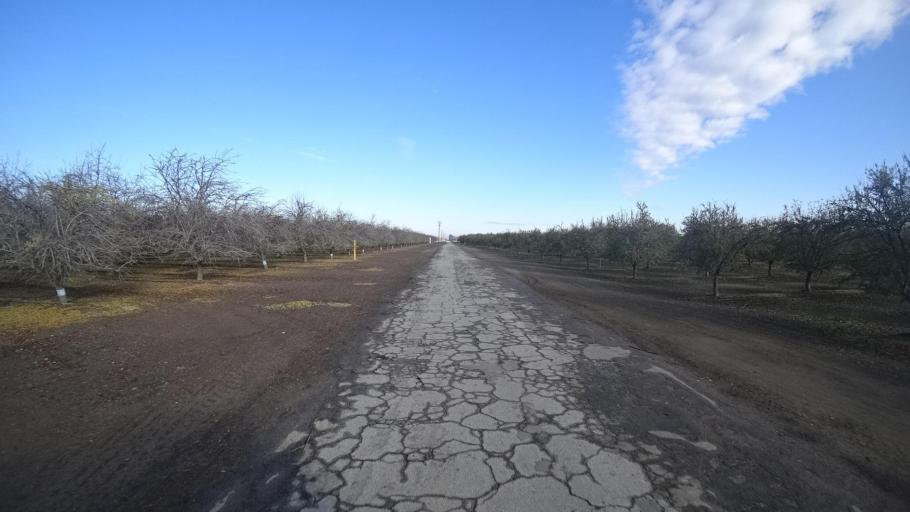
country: US
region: California
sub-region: Kern County
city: McFarland
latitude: 35.7051
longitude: -119.3208
